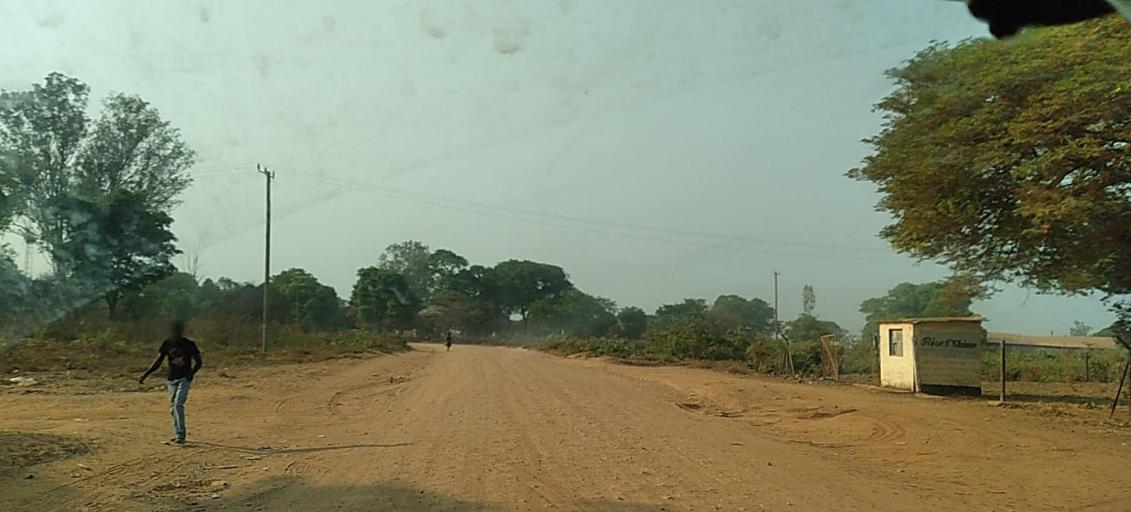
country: ZM
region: North-Western
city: Kabompo
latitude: -13.5947
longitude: 24.2030
